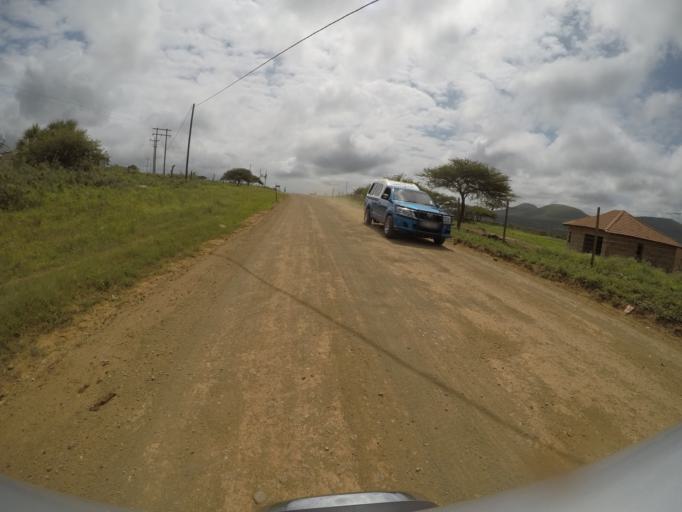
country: ZA
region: KwaZulu-Natal
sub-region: uThungulu District Municipality
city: Empangeni
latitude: -28.5795
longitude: 31.8478
